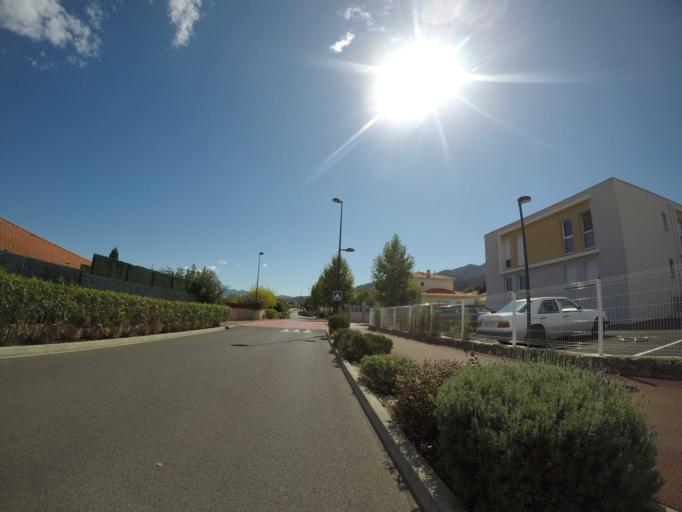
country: FR
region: Languedoc-Roussillon
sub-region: Departement des Pyrenees-Orientales
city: Ceret
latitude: 42.4924
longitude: 2.7374
